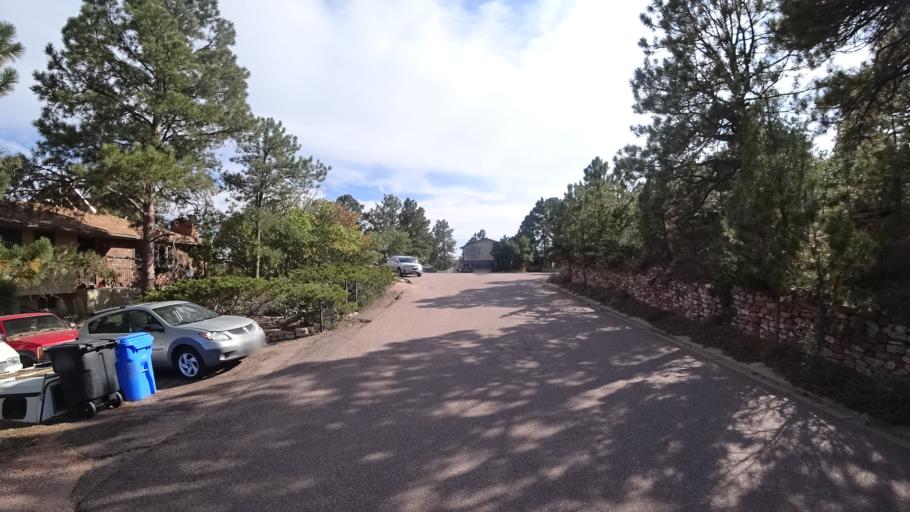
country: US
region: Colorado
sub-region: El Paso County
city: Colorado Springs
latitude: 38.8941
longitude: -104.7743
